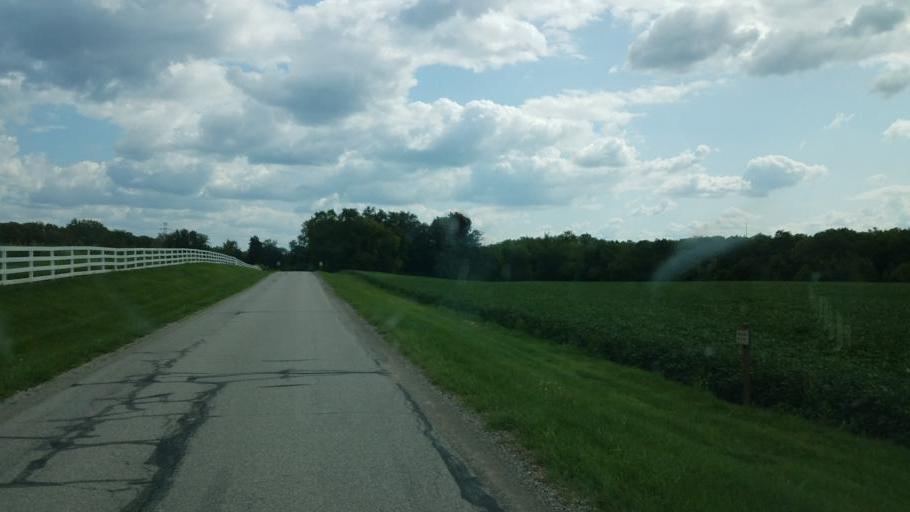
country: US
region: Ohio
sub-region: Delaware County
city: Lewis Center
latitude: 40.2244
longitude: -83.0613
